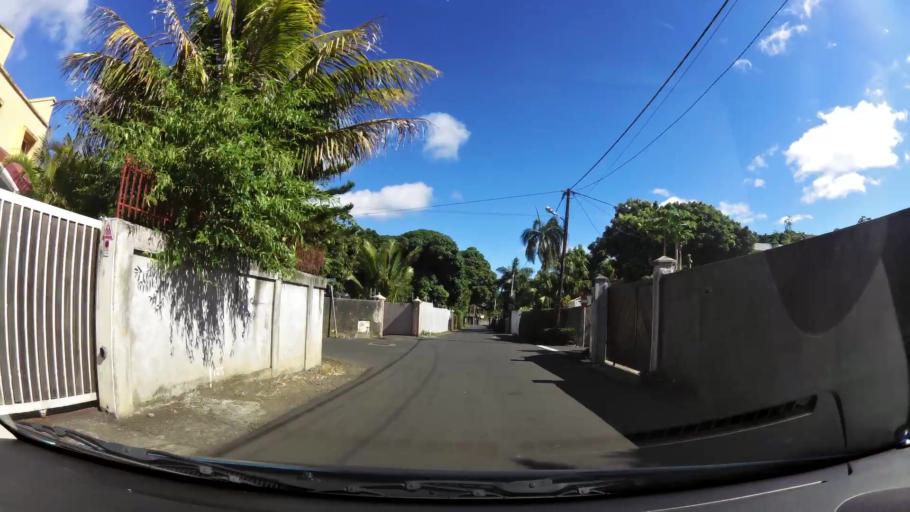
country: MU
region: Plaines Wilhems
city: Vacoas
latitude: -20.2993
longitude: 57.4880
